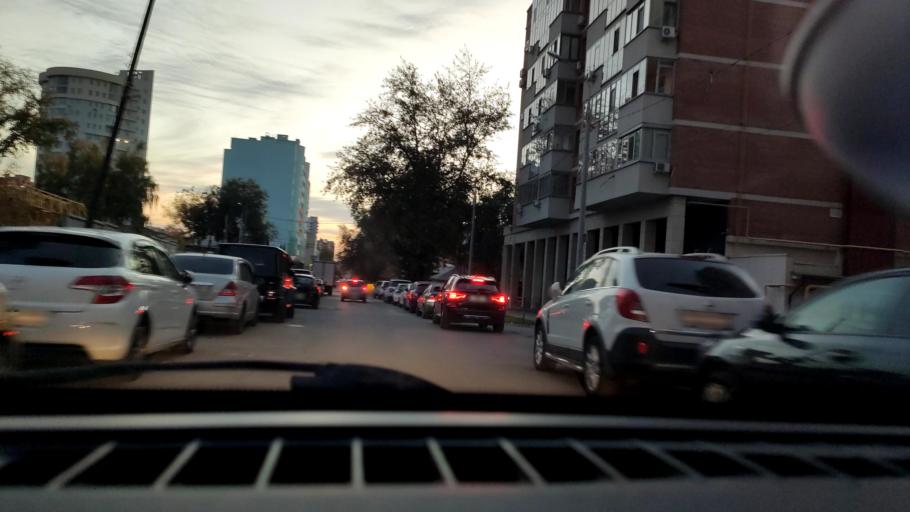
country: RU
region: Samara
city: Samara
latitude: 53.2012
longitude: 50.1249
